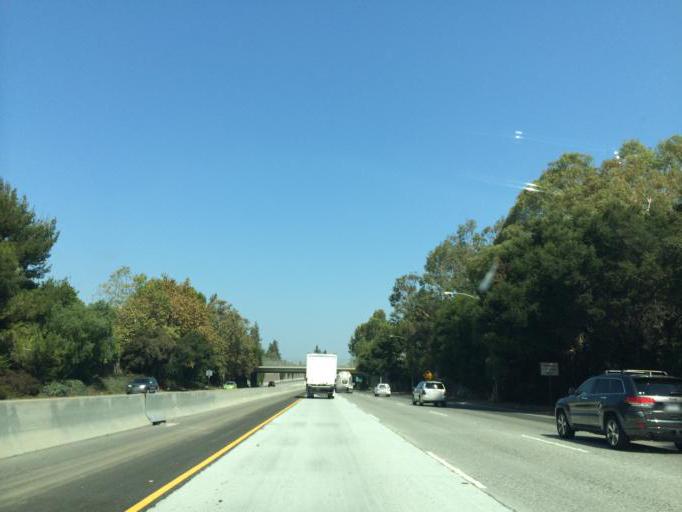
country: US
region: California
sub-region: Santa Clara County
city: Mountain View
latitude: 37.3972
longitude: -122.0690
